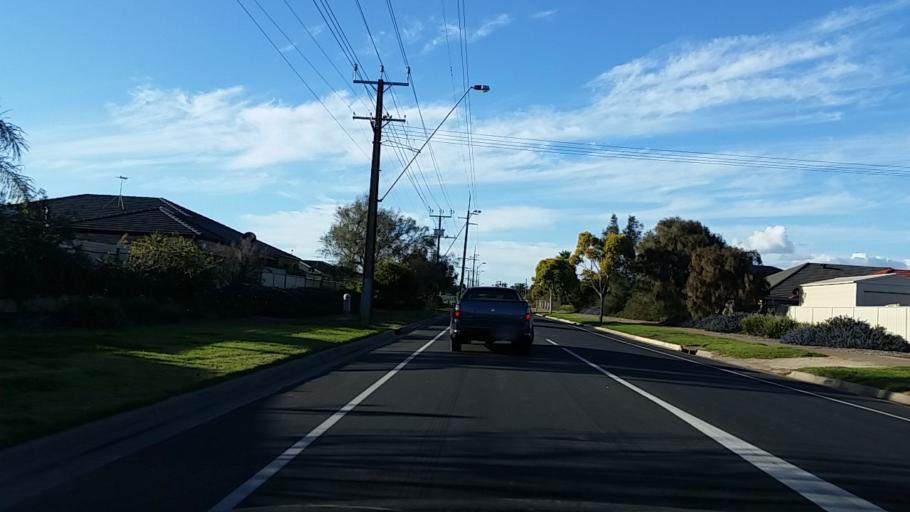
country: AU
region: South Australia
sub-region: Salisbury
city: Salisbury
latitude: -34.7887
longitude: 138.6020
